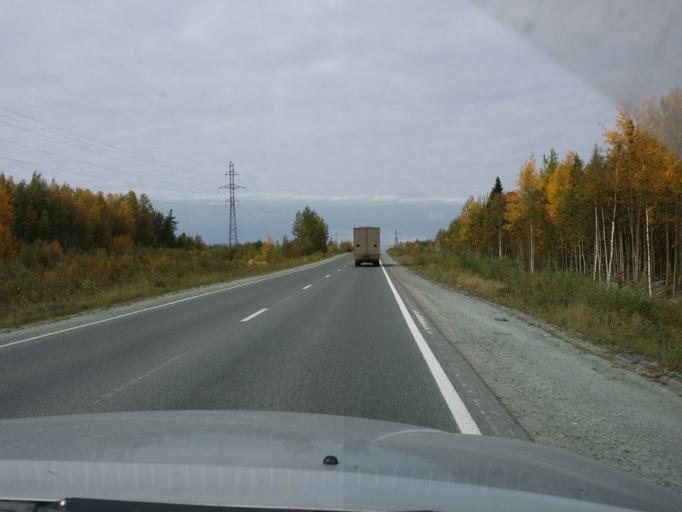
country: RU
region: Khanty-Mansiyskiy Avtonomnyy Okrug
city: Megion
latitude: 61.1026
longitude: 75.9532
